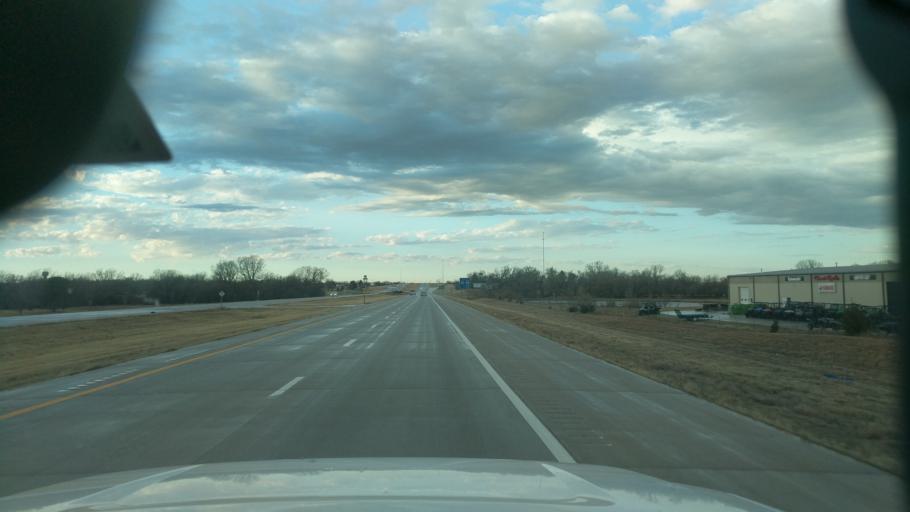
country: US
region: Kansas
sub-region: Harvey County
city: Hesston
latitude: 38.1382
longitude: -97.4093
